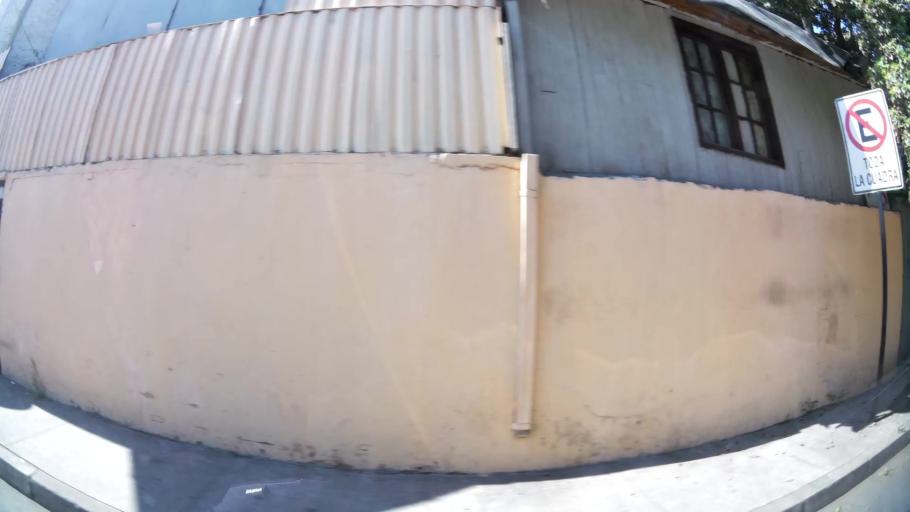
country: CL
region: Santiago Metropolitan
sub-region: Provincia de Santiago
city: Santiago
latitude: -33.4286
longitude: -70.6715
